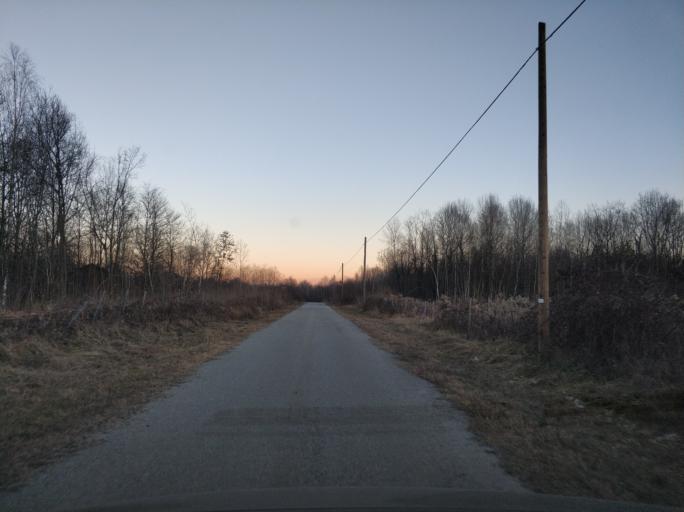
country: IT
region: Piedmont
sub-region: Provincia di Torino
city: Vauda Canavese Superiore
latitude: 45.2671
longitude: 7.6130
